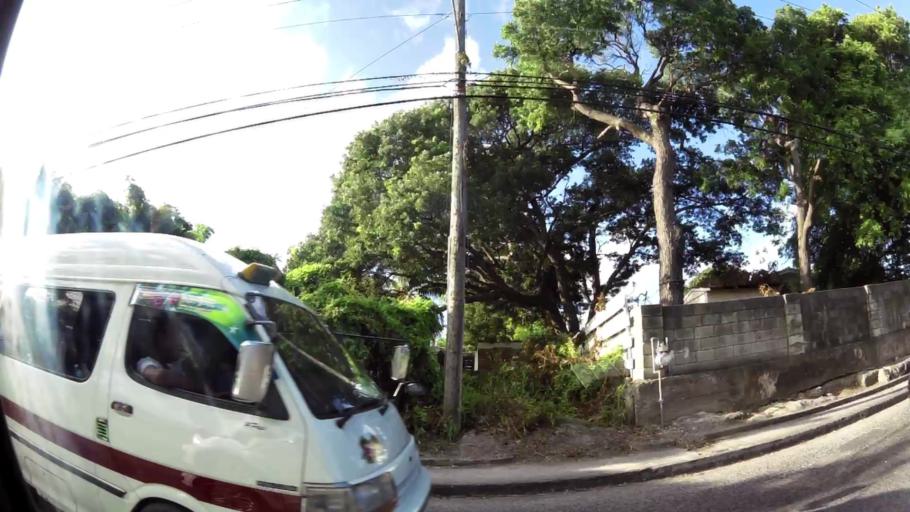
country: BB
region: Saint Michael
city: Bridgetown
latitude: 13.0922
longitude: -59.5896
